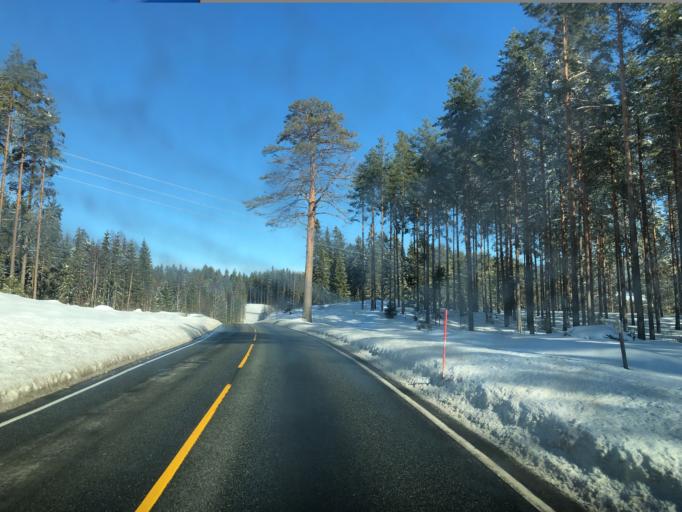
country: NO
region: Oppland
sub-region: Jevnaker
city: Jevnaker
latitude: 60.2274
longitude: 10.3914
